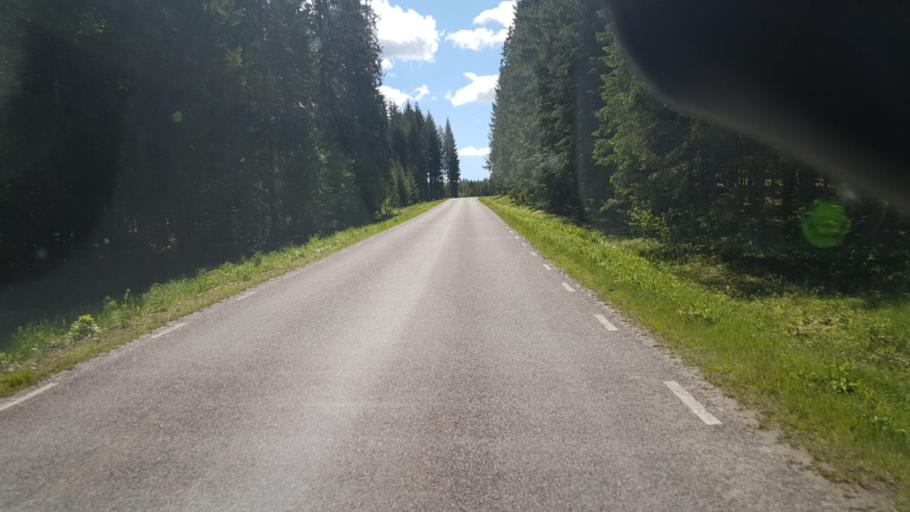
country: SE
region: Vaermland
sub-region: Grums Kommun
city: Grums
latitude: 59.4999
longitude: 12.8759
